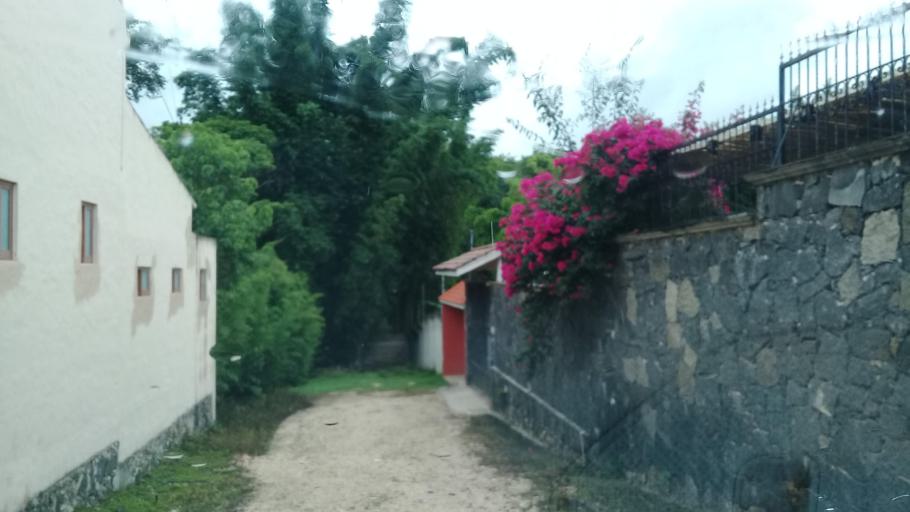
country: MX
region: Veracruz
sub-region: Emiliano Zapata
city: Jacarandas
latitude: 19.5043
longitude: -96.8410
